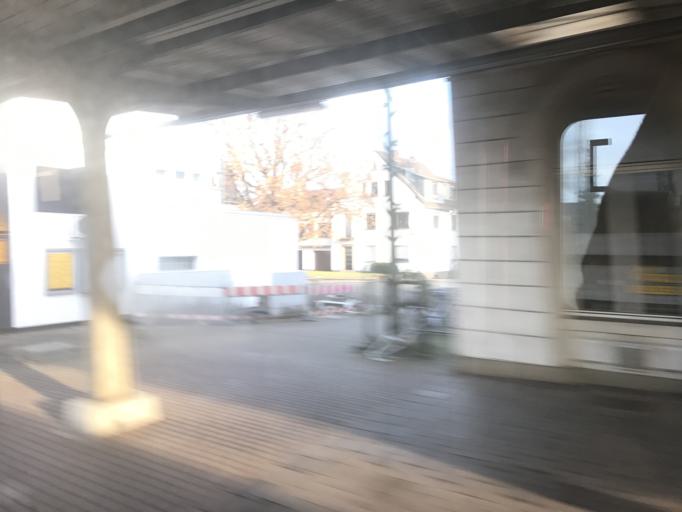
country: DE
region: Rheinland-Pfalz
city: Weissenthurm
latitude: 50.4213
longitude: 7.4509
